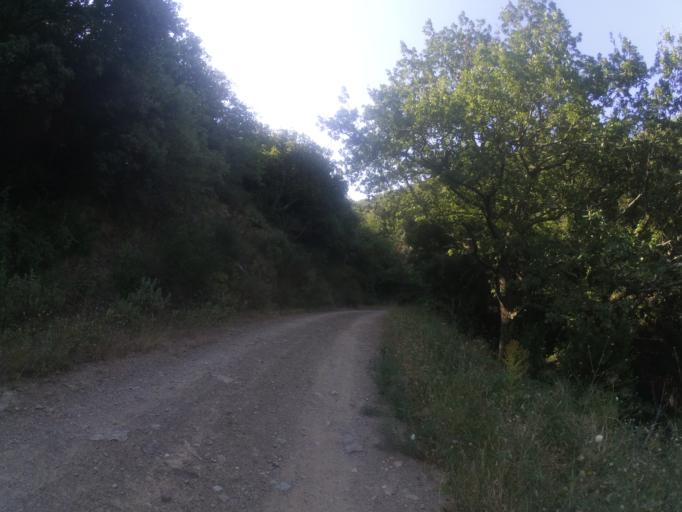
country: FR
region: Languedoc-Roussillon
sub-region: Departement des Pyrenees-Orientales
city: Ille-sur-Tet
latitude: 42.6493
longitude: 2.6436
